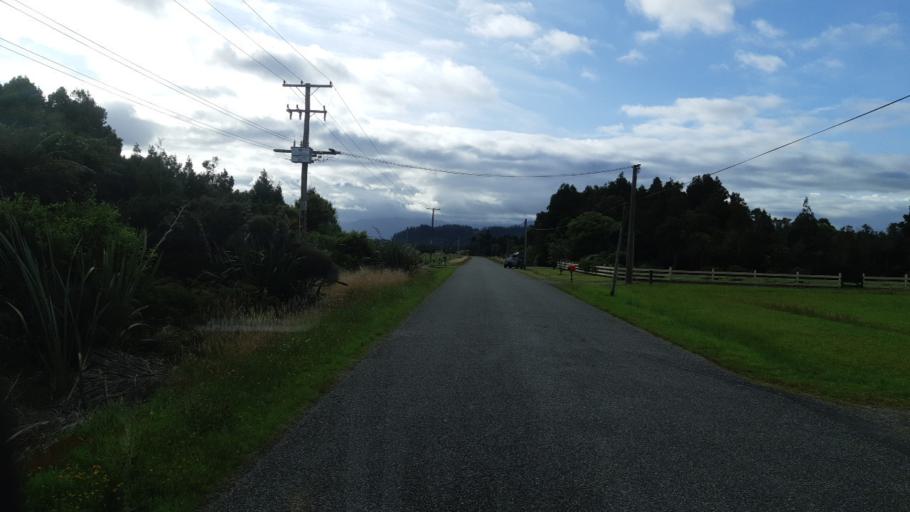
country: NZ
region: West Coast
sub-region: Westland District
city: Hokitika
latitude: -42.7309
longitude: 170.9616
